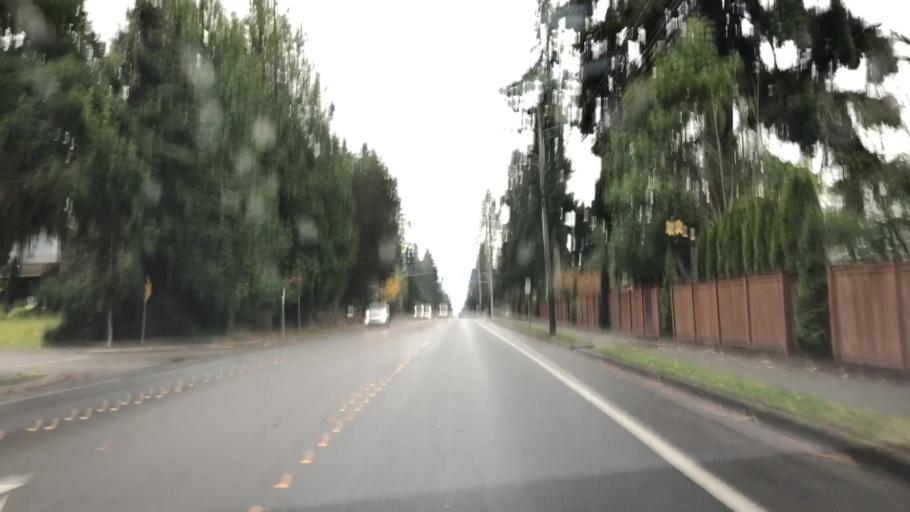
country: US
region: Washington
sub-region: Snohomish County
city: Alderwood Manor
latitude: 47.8403
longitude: -122.2925
